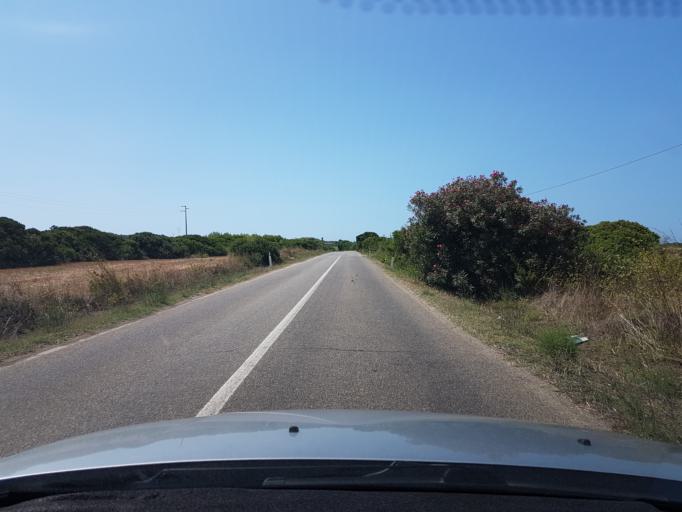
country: IT
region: Sardinia
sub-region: Provincia di Oristano
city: Riola Sardo
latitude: 40.0246
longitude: 8.4414
